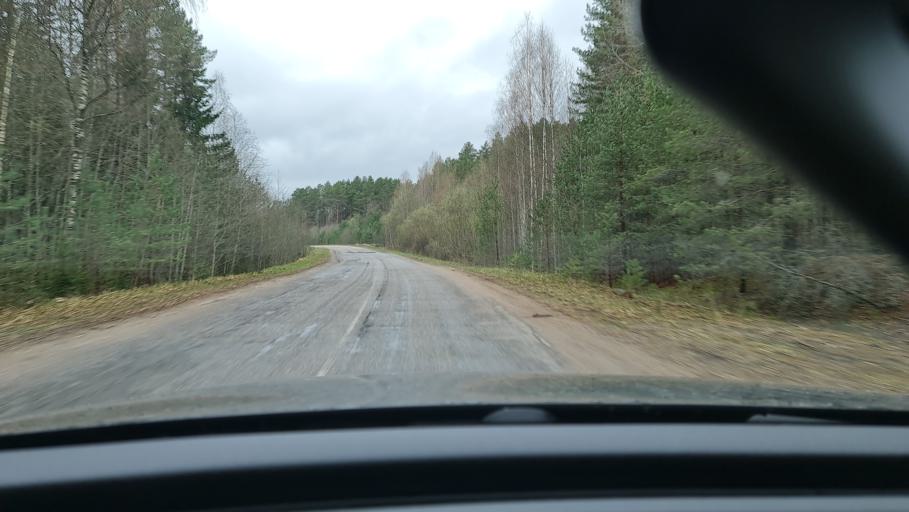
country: RU
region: Novgorod
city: Marevo
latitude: 57.1009
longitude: 31.7270
